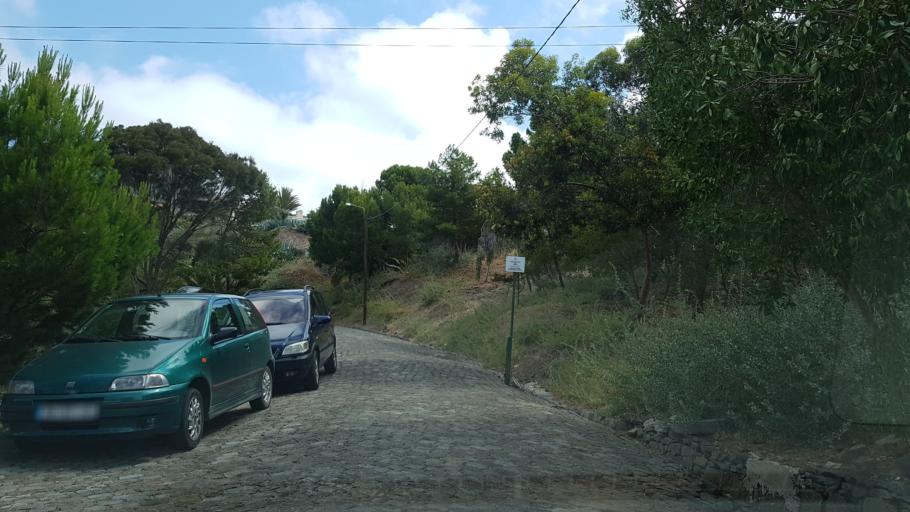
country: PT
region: Madeira
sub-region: Porto Santo
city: Vila de Porto Santo
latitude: 33.0651
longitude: -16.3340
